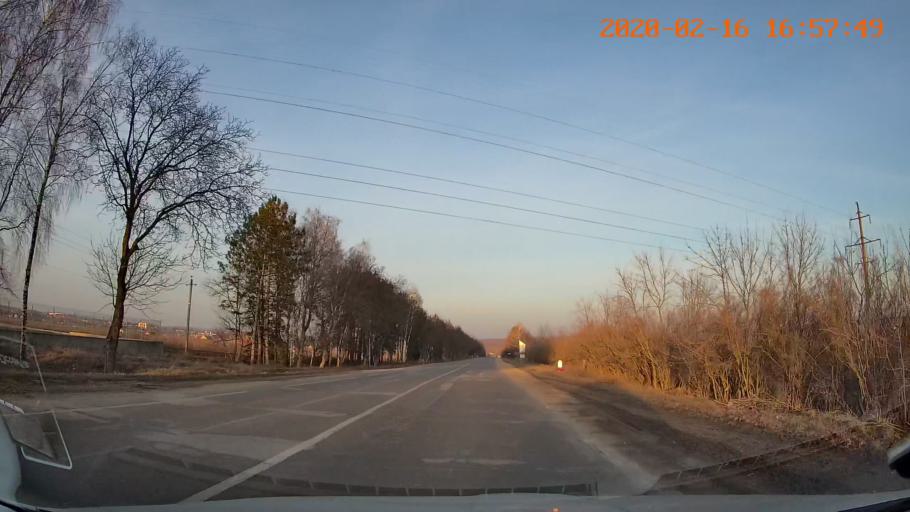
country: MD
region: Briceni
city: Briceni
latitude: 48.3462
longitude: 27.0740
